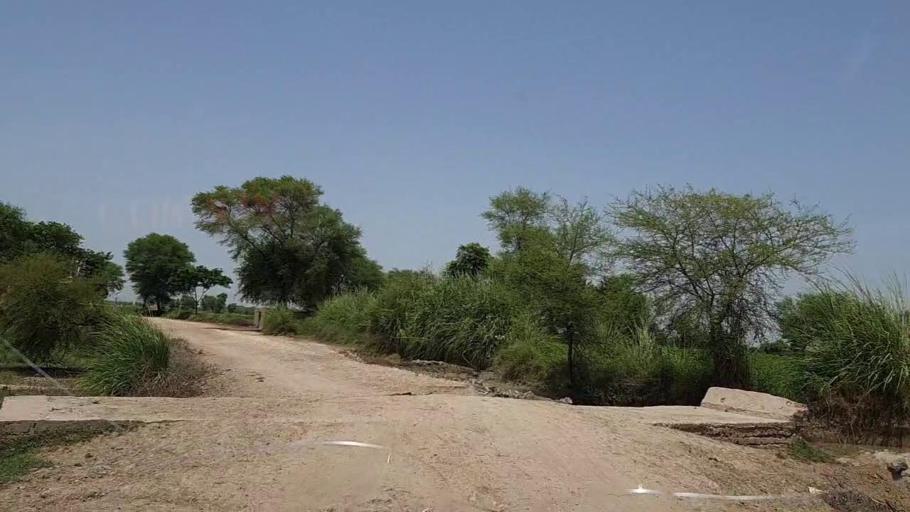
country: PK
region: Sindh
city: Tharu Shah
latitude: 26.9151
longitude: 68.0605
